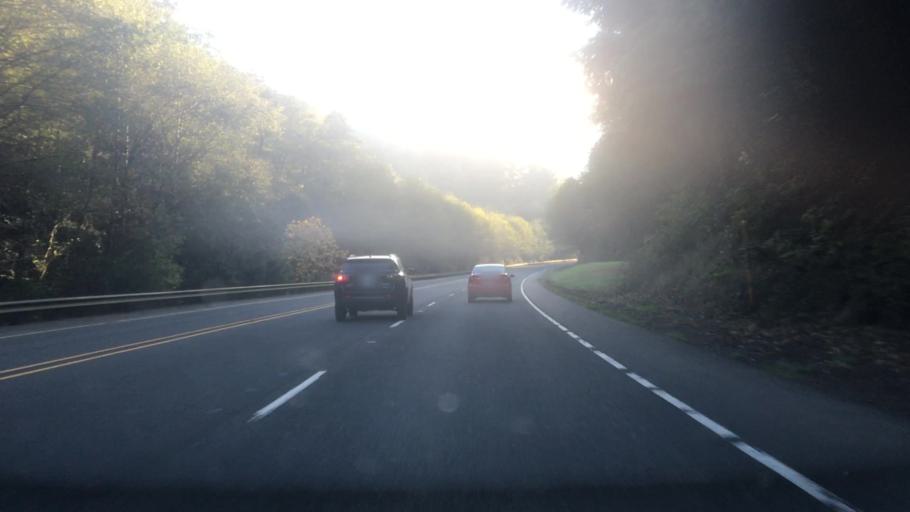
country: US
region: Oregon
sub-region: Clatsop County
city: Cannon Beach
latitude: 45.9242
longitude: -123.9316
